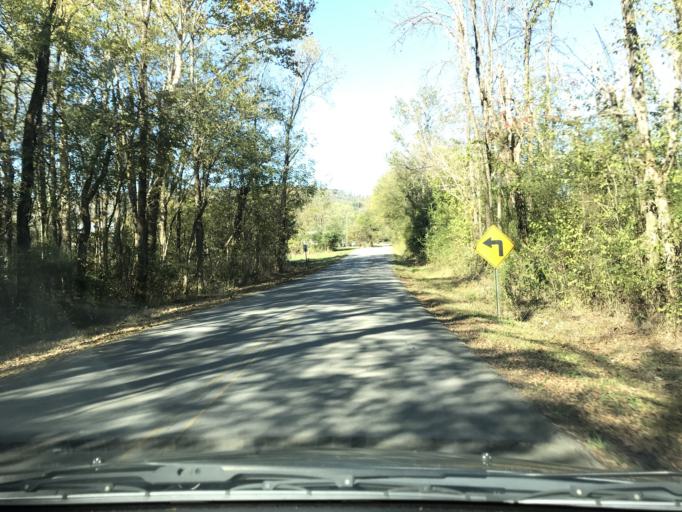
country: US
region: Georgia
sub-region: Dade County
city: Trenton
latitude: 34.9108
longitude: -85.4740
